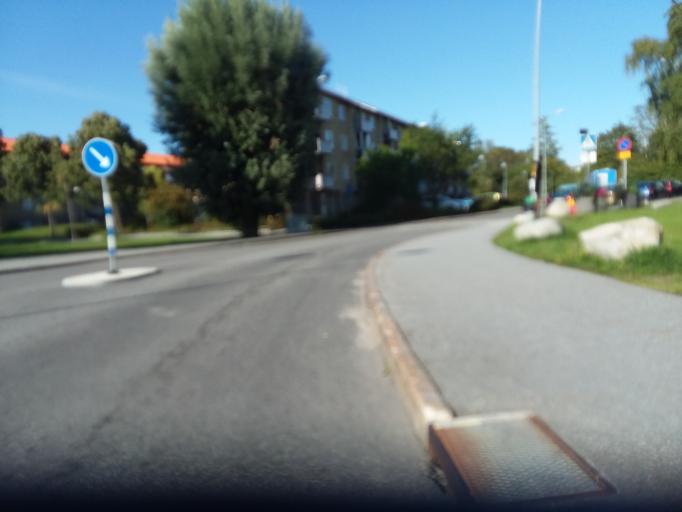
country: SE
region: Stockholm
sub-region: Stockholms Kommun
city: Bromma
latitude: 59.3565
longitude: 17.8720
